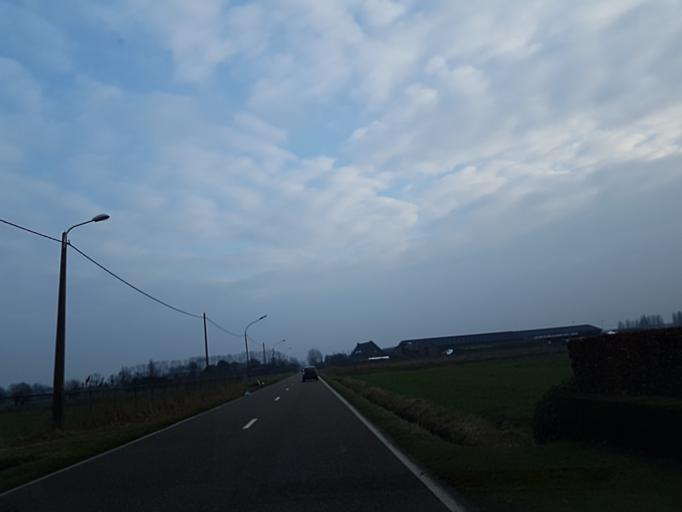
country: BE
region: Flanders
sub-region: Provincie Antwerpen
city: Stabroek
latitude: 51.3155
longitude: 4.3829
